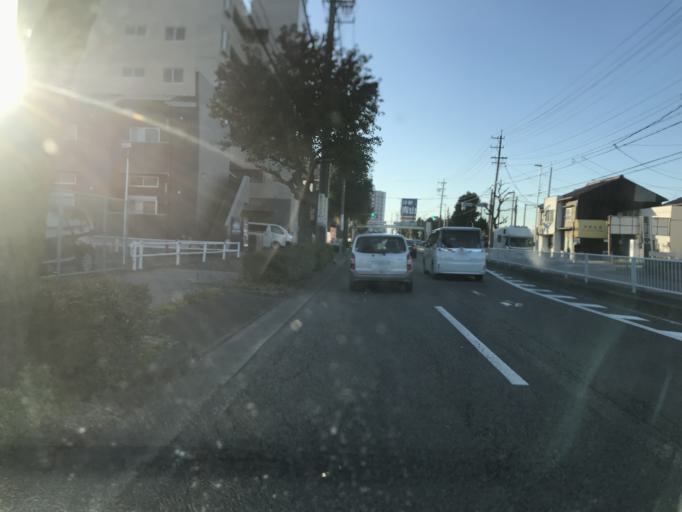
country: JP
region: Aichi
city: Nagoya-shi
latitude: 35.1772
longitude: 136.8525
